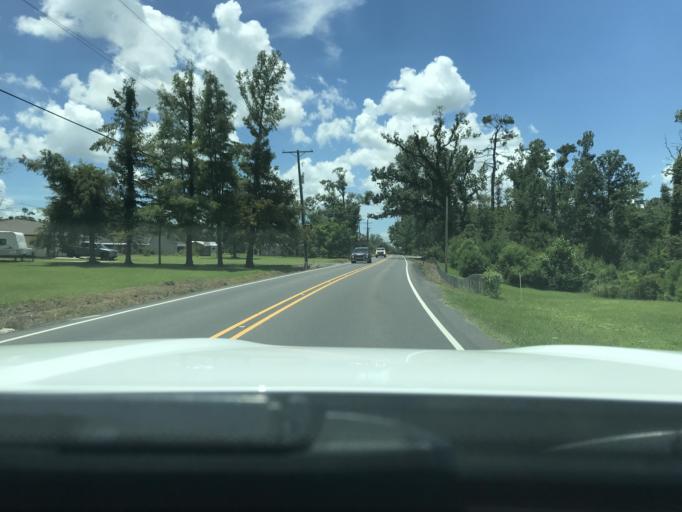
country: US
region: Louisiana
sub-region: Calcasieu Parish
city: Moss Bluff
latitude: 30.3041
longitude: -93.1809
